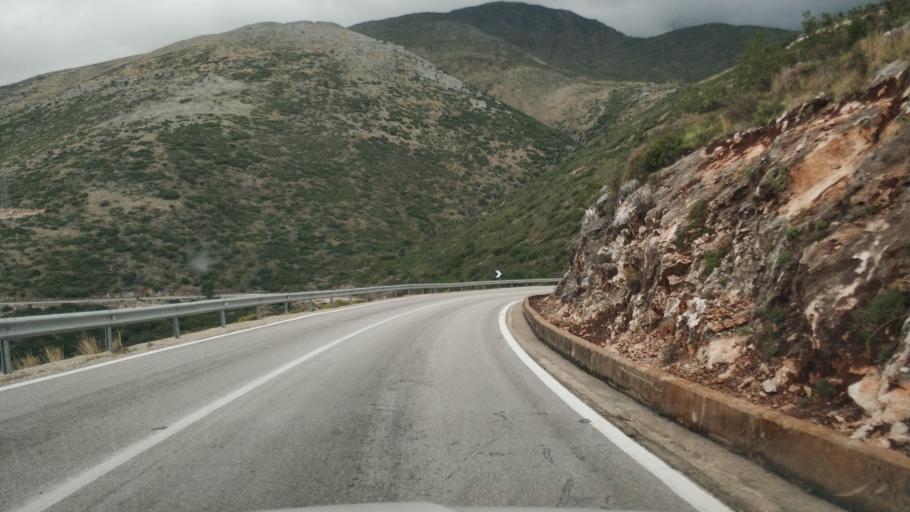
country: AL
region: Vlore
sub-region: Rrethi i Vlores
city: Vranisht
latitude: 40.1423
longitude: 19.6614
